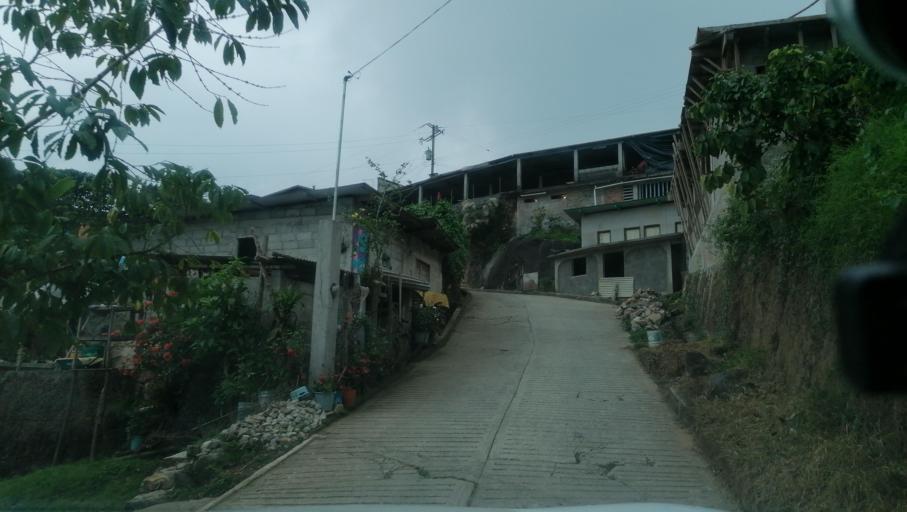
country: MX
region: Chiapas
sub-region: Cacahoatan
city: Benito Juarez
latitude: 15.0857
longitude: -92.1612
